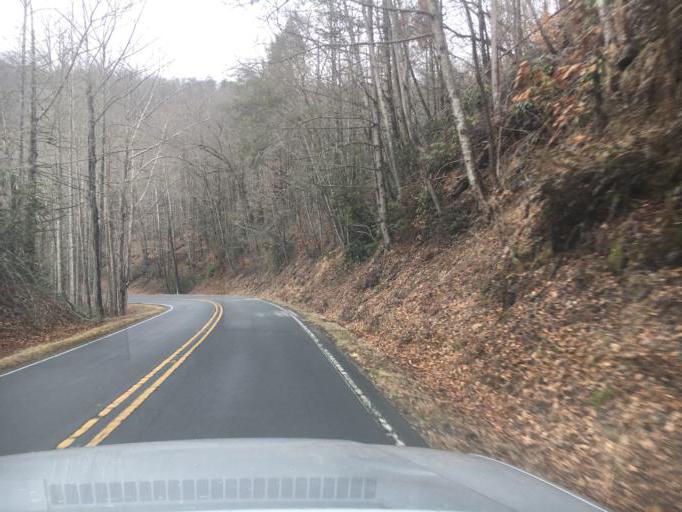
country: US
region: North Carolina
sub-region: Transylvania County
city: Brevard
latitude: 35.2879
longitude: -82.7494
